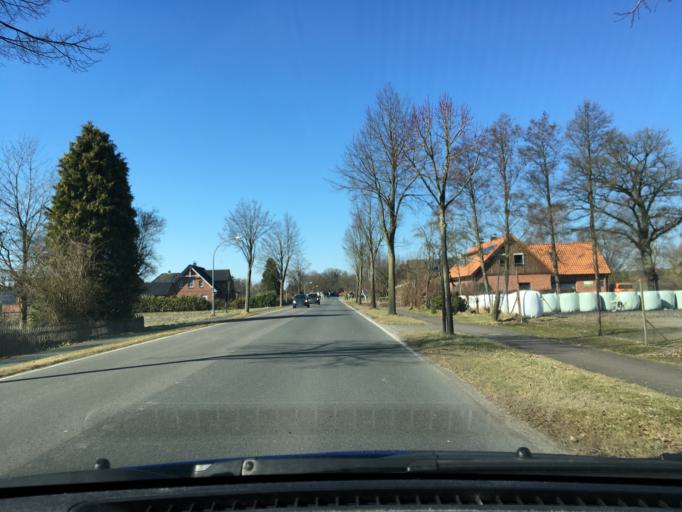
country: DE
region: Lower Saxony
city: Brockel
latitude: 53.0956
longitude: 9.5174
